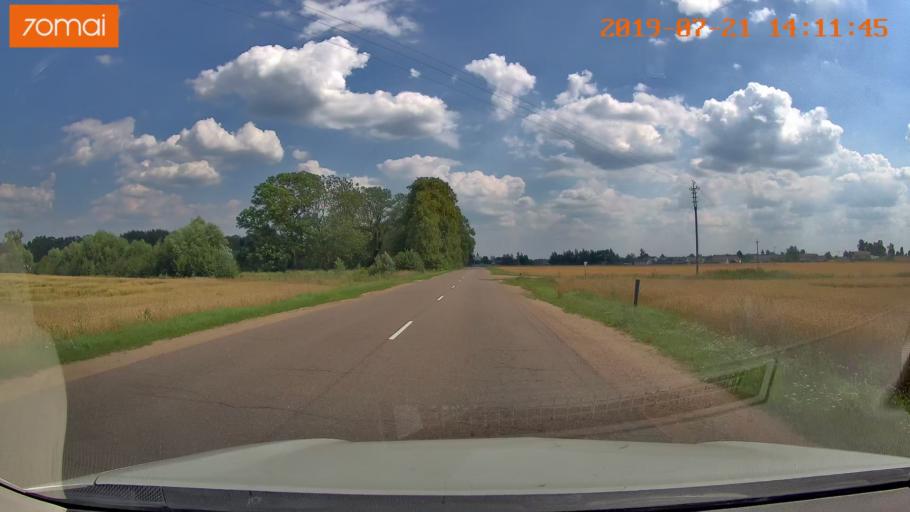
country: BY
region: Grodnenskaya
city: Karelichy
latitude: 53.6555
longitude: 26.1589
